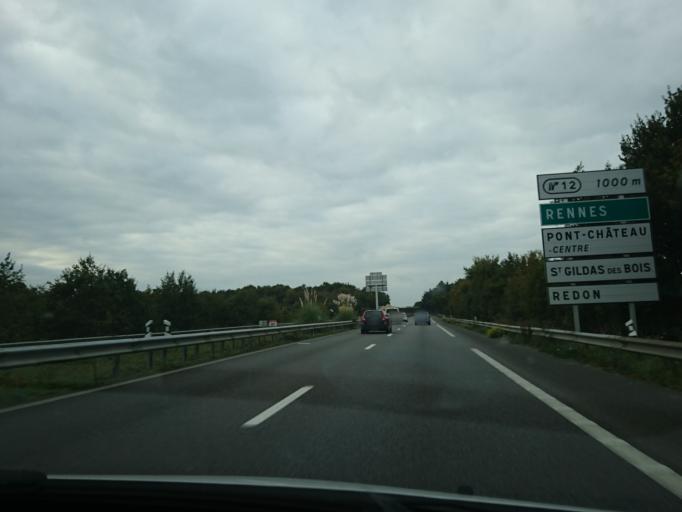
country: FR
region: Pays de la Loire
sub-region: Departement de la Loire-Atlantique
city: Pontchateau
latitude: 47.4398
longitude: -2.0767
